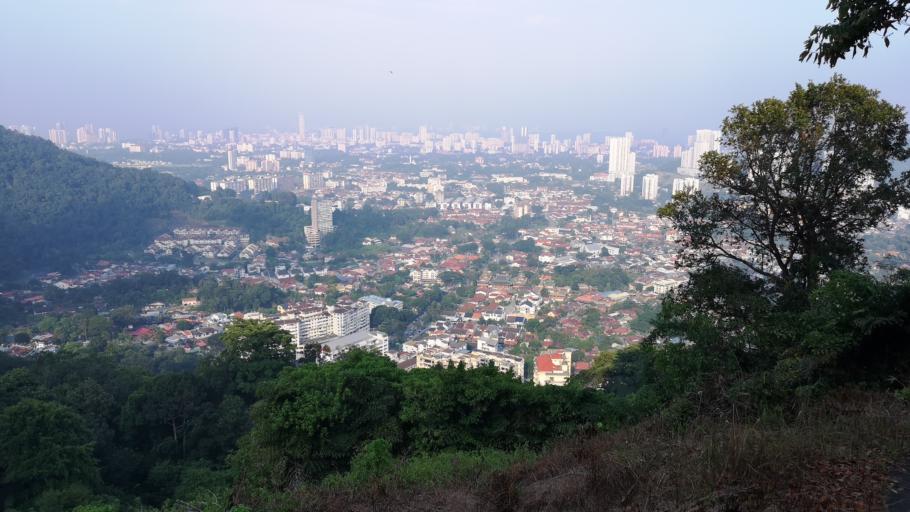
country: MY
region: Penang
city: George Town
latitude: 5.4074
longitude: 100.2723
